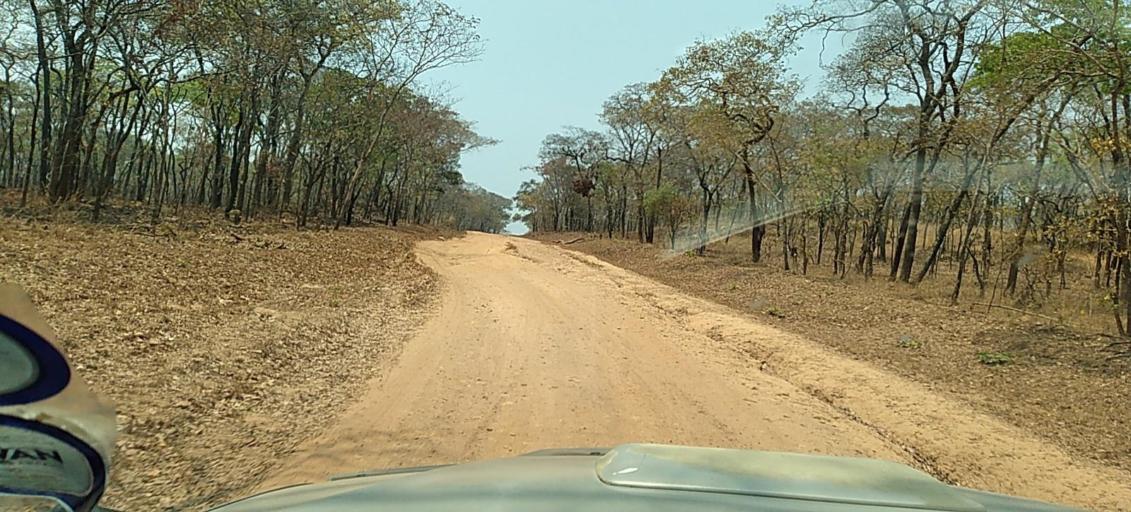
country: ZM
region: North-Western
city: Kasempa
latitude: -13.5537
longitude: 26.0660
